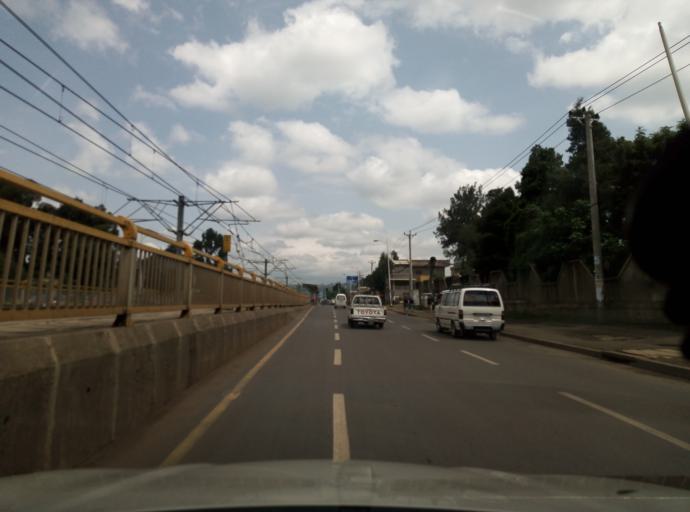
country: ET
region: Adis Abeba
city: Addis Ababa
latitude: 9.0110
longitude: 38.7239
